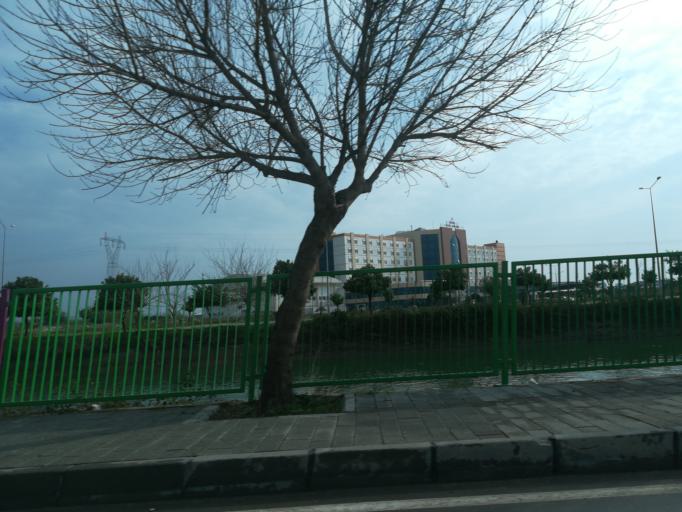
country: TR
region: Adana
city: Adana
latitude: 37.0107
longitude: 35.3519
